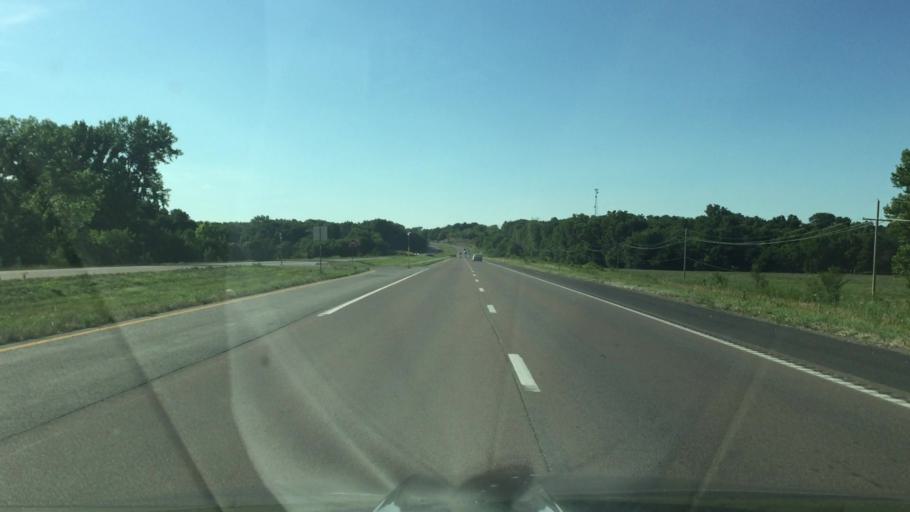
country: US
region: Missouri
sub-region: Pettis County
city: Sedalia
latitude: 38.7244
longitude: -93.3019
